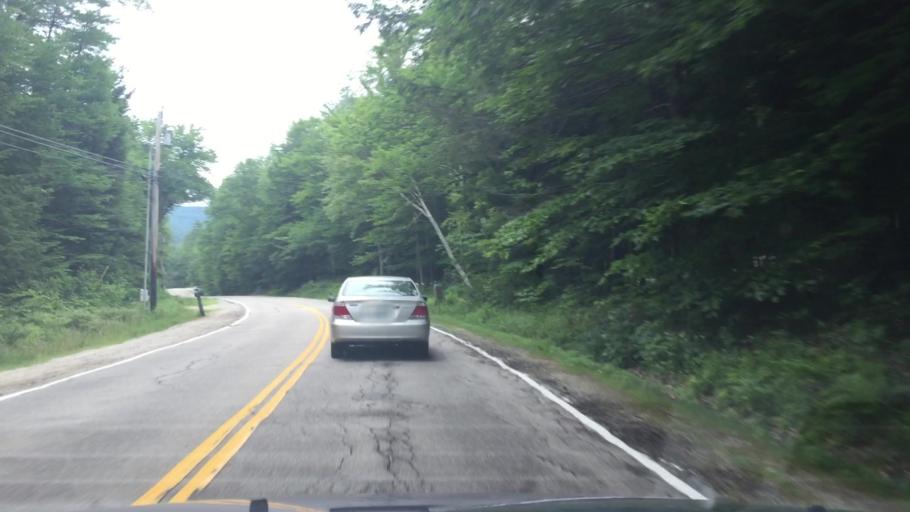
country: US
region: New Hampshire
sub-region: Carroll County
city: Conway
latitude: 43.9325
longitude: -71.0868
